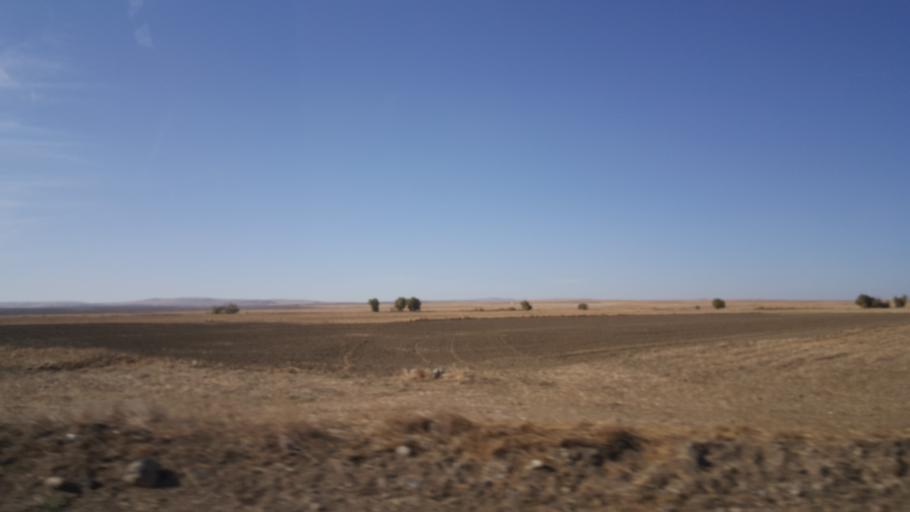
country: TR
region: Ankara
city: Yenice
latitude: 39.3725
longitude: 32.8131
